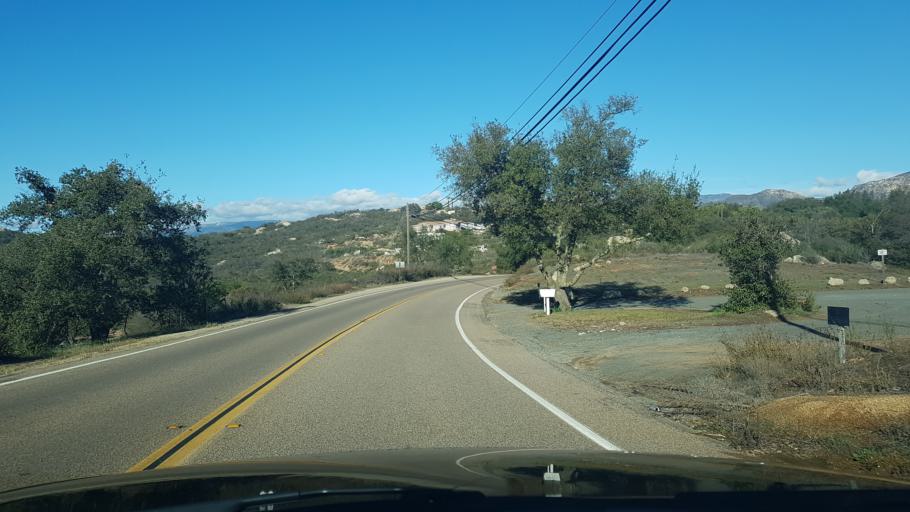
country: US
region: California
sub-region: San Diego County
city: Valley Center
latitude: 33.2045
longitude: -116.9556
